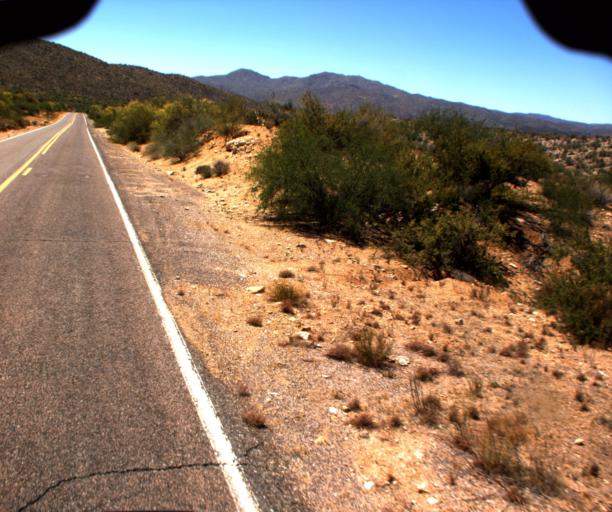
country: US
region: Arizona
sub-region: Yavapai County
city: Bagdad
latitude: 34.4609
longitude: -113.0268
